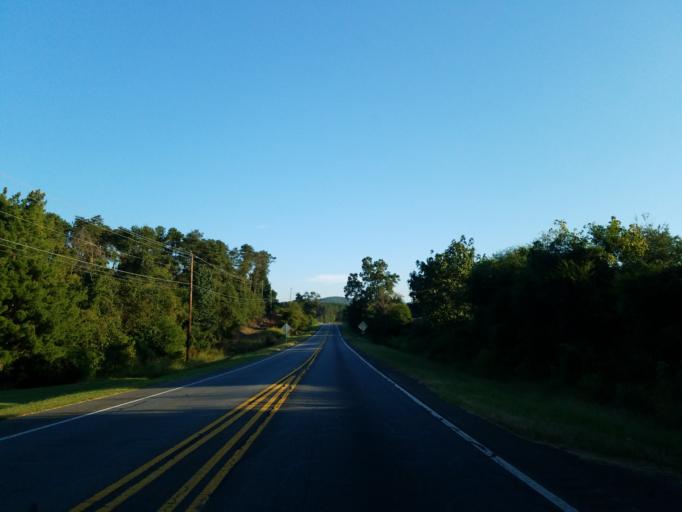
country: US
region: Georgia
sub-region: Bartow County
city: Rydal
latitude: 34.3413
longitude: -84.7177
